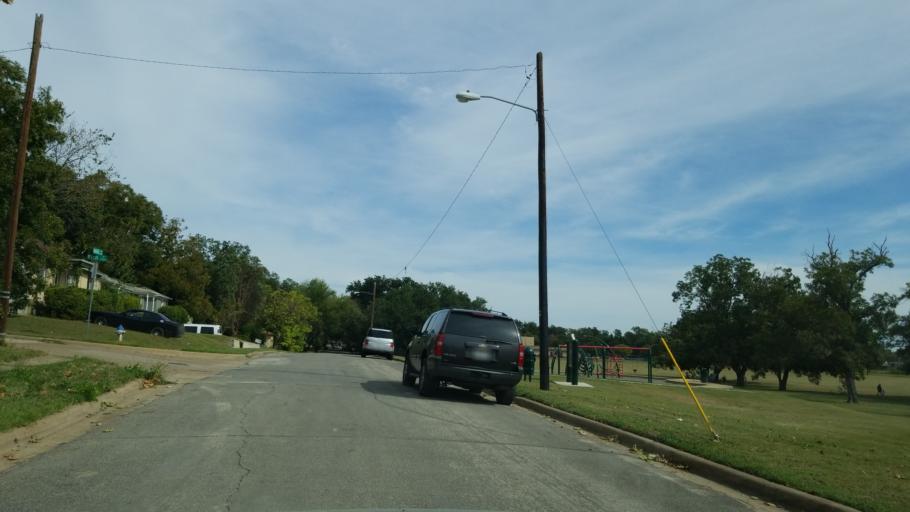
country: US
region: Texas
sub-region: Dallas County
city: Dallas
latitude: 32.7682
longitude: -96.7246
